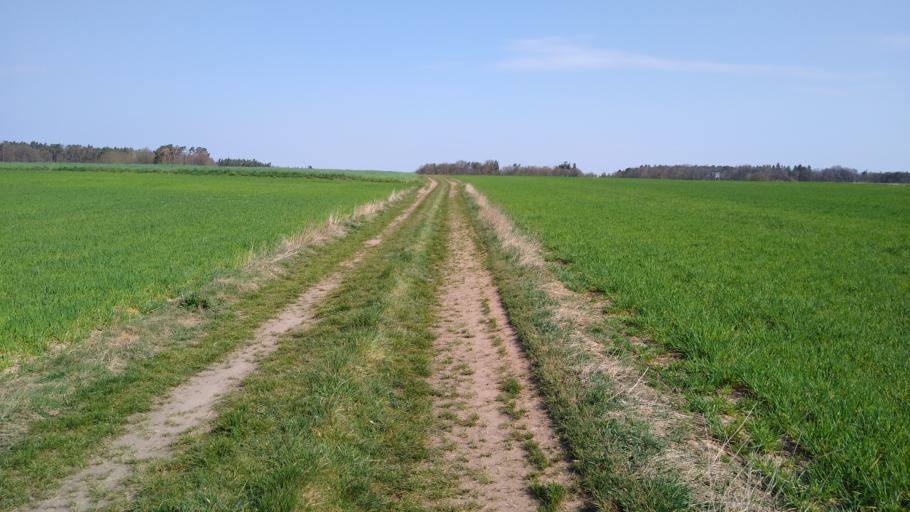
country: DE
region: Bavaria
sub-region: Regierungsbezirk Mittelfranken
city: Obermichelbach
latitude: 49.4972
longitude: 10.9223
